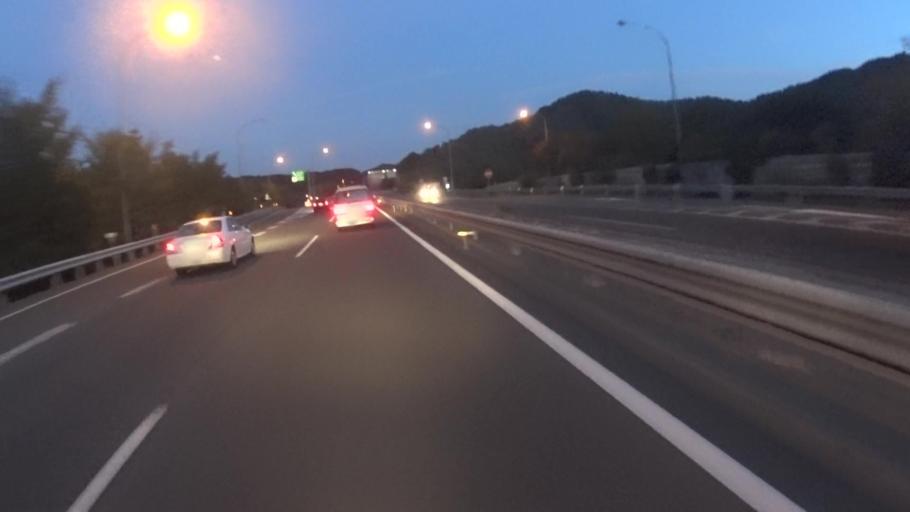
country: JP
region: Kyoto
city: Kameoka
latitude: 35.0993
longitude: 135.4953
